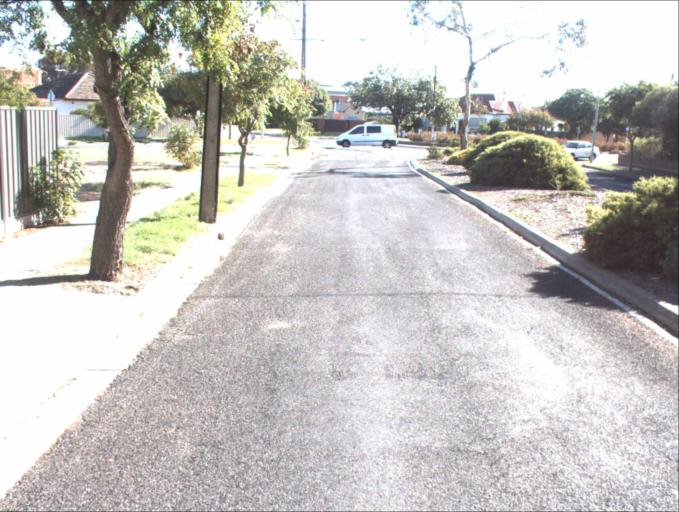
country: AU
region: South Australia
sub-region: Port Adelaide Enfield
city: Klemzig
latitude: -34.8768
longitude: 138.6149
